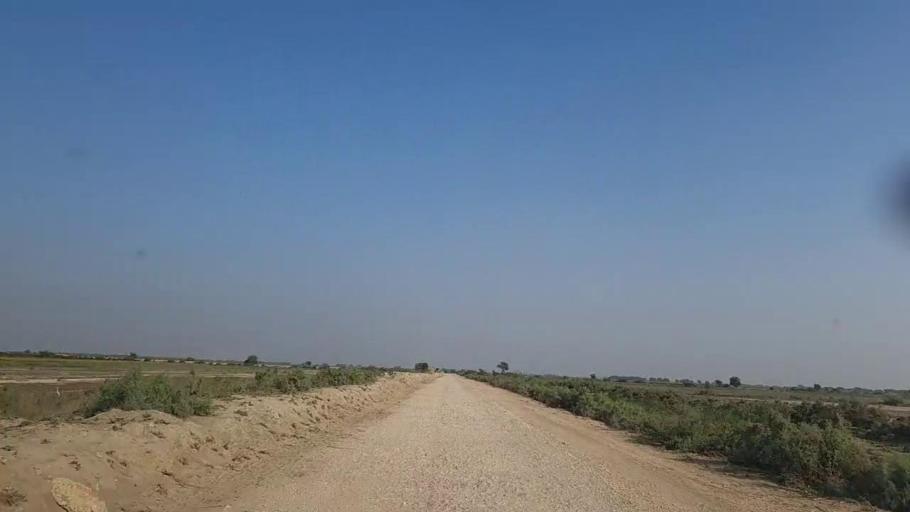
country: PK
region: Sindh
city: Jati
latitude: 24.4603
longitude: 68.2875
